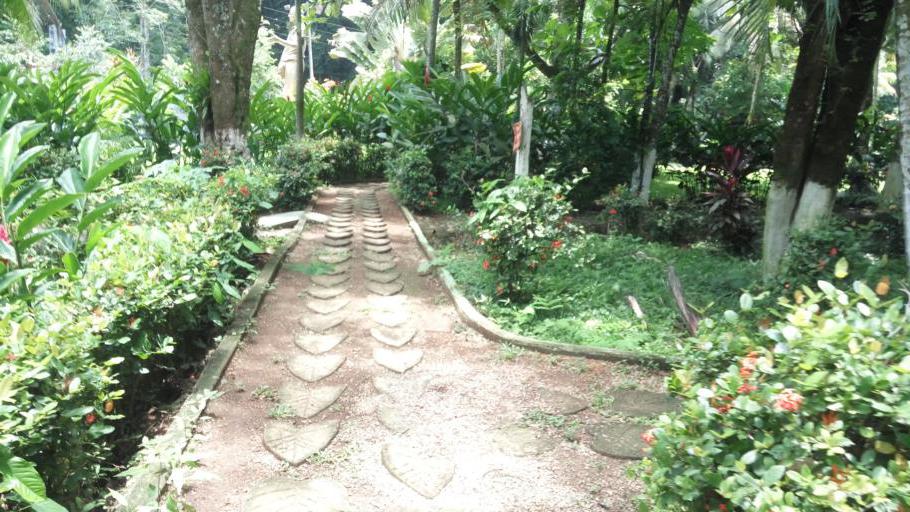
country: MX
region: Tabasco
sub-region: Teapa
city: Eureka y Belen
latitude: 17.5634
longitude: -92.9288
